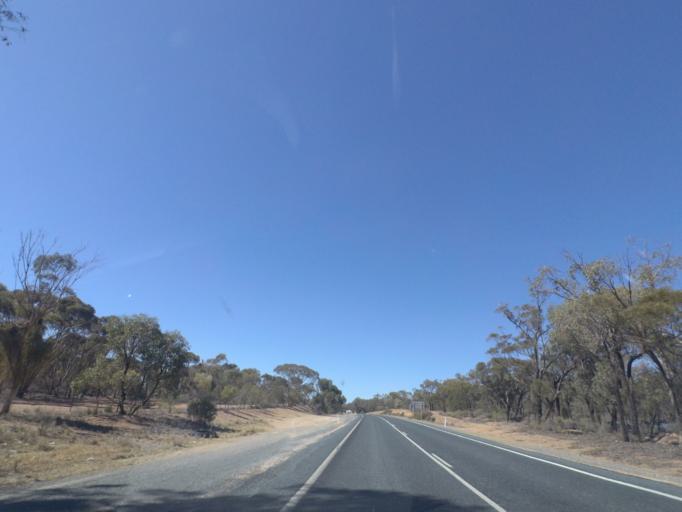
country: AU
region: New South Wales
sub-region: Bland
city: West Wyalong
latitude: -34.1374
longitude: 147.1212
